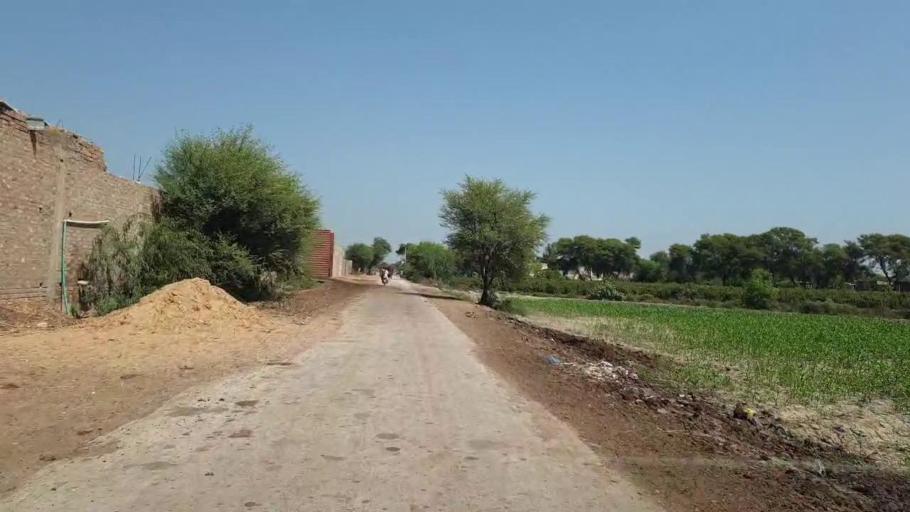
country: PK
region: Sindh
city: Hyderabad
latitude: 25.4501
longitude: 68.4154
